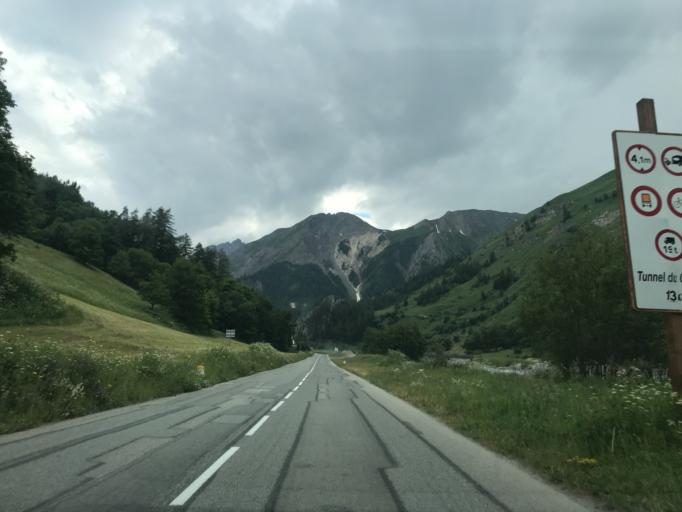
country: FR
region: Rhone-Alpes
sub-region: Departement de la Savoie
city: Valloire
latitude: 45.1350
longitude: 6.4195
